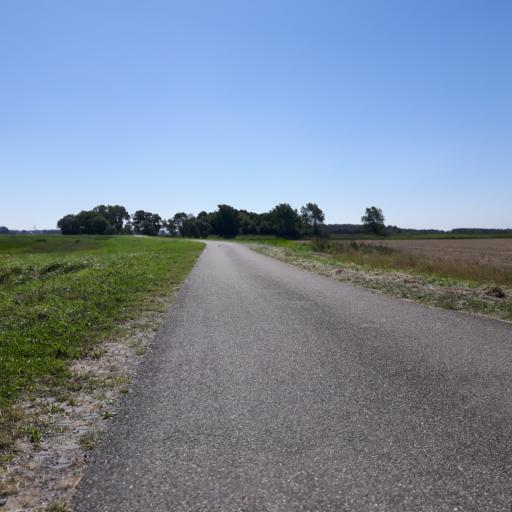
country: NL
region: Zeeland
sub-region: Gemeente Noord-Beveland
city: Kamperland
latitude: 51.5966
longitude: 3.7759
